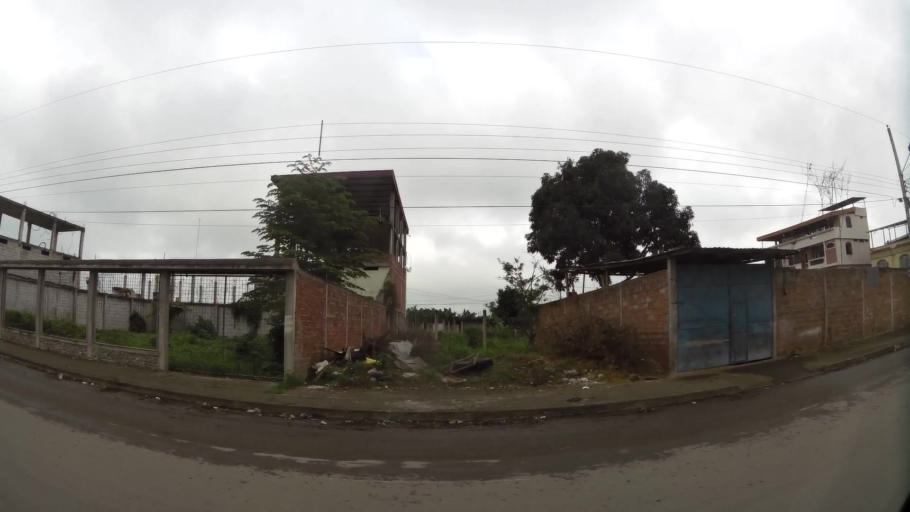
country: EC
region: El Oro
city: Pasaje
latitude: -3.3237
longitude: -79.8148
